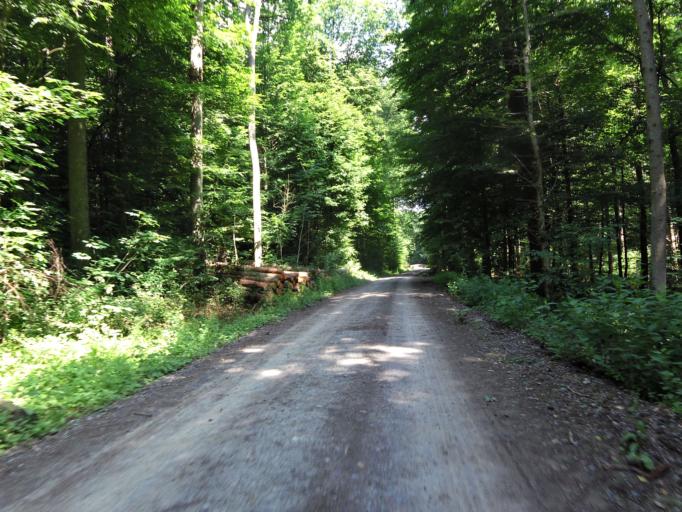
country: DE
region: Bavaria
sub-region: Regierungsbezirk Unterfranken
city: Wuerzburg
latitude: 49.7605
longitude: 9.9009
